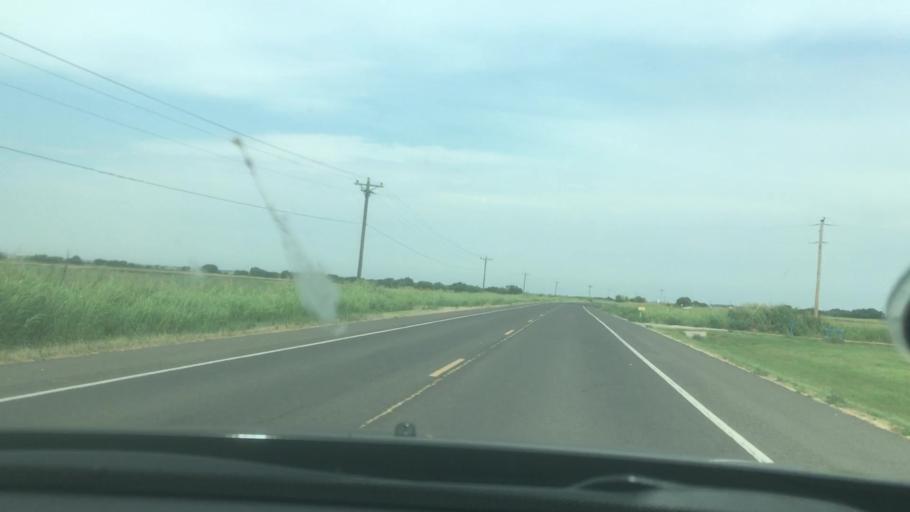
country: US
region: Oklahoma
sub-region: Garvin County
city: Maysville
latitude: 34.8192
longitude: -97.4833
